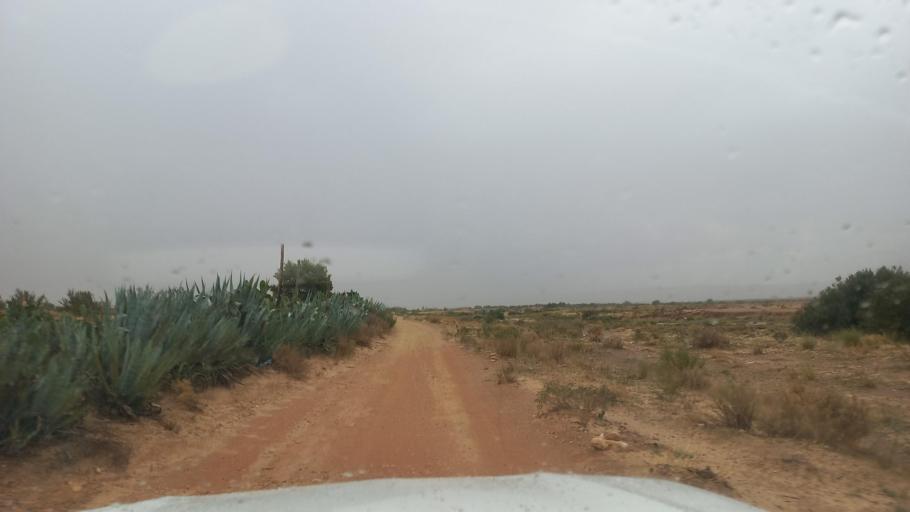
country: TN
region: Al Qasrayn
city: Kasserine
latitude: 35.2695
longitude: 8.9465
